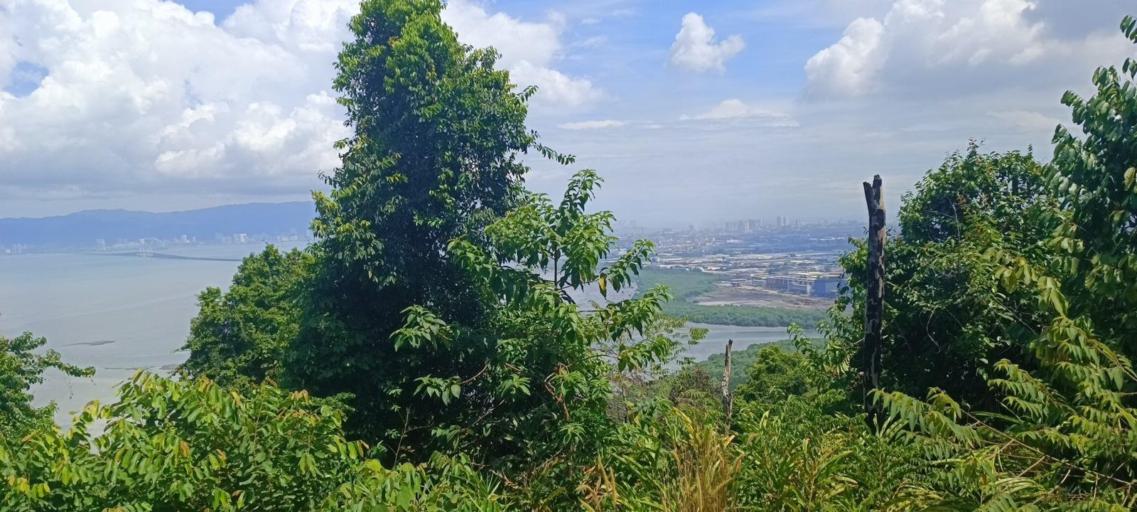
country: MY
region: Penang
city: Juru
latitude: 5.3282
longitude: 100.4095
